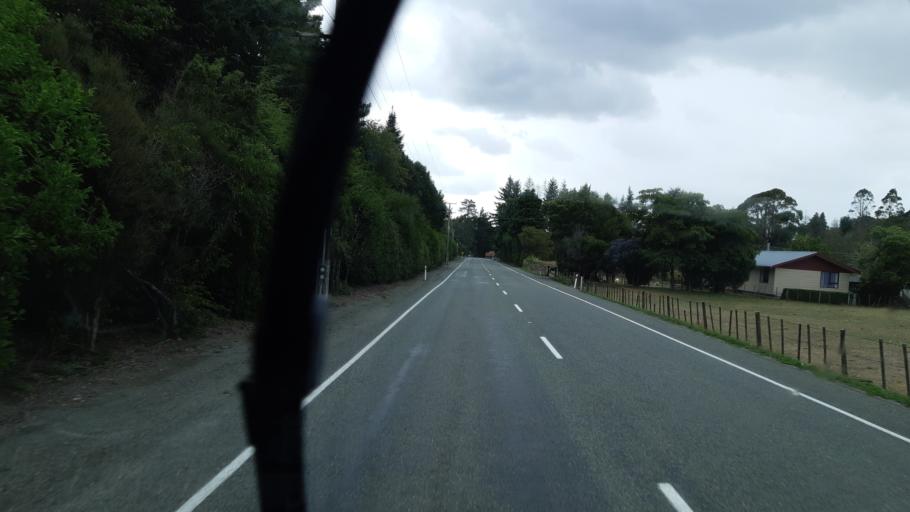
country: NZ
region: Tasman
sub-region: Tasman District
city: Wakefield
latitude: -41.4123
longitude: 173.0181
